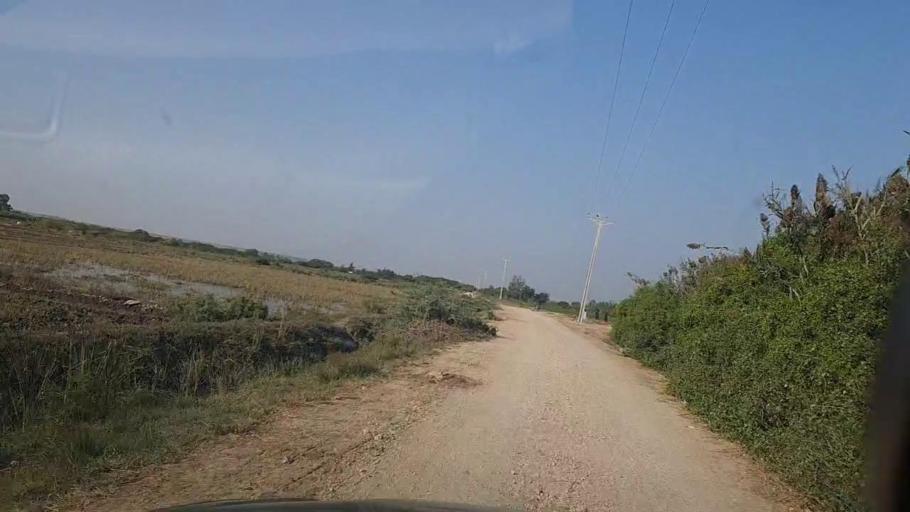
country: PK
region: Sindh
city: Thatta
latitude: 24.6042
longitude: 67.8744
